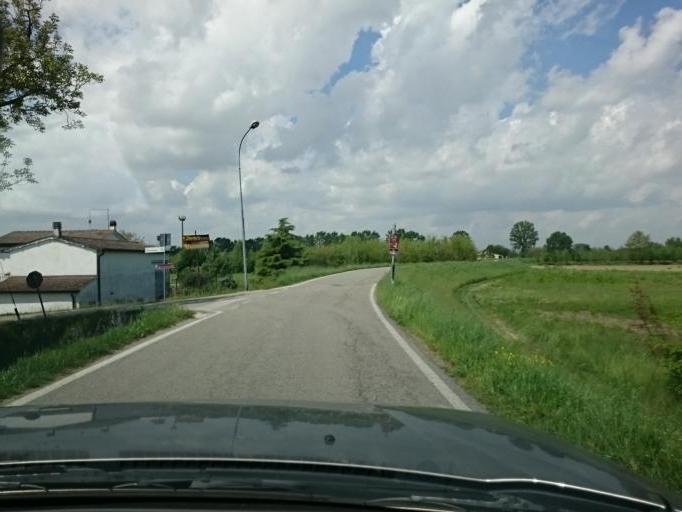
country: IT
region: Veneto
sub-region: Provincia di Padova
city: Cervarese Santa Croce
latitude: 45.4167
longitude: 11.7068
